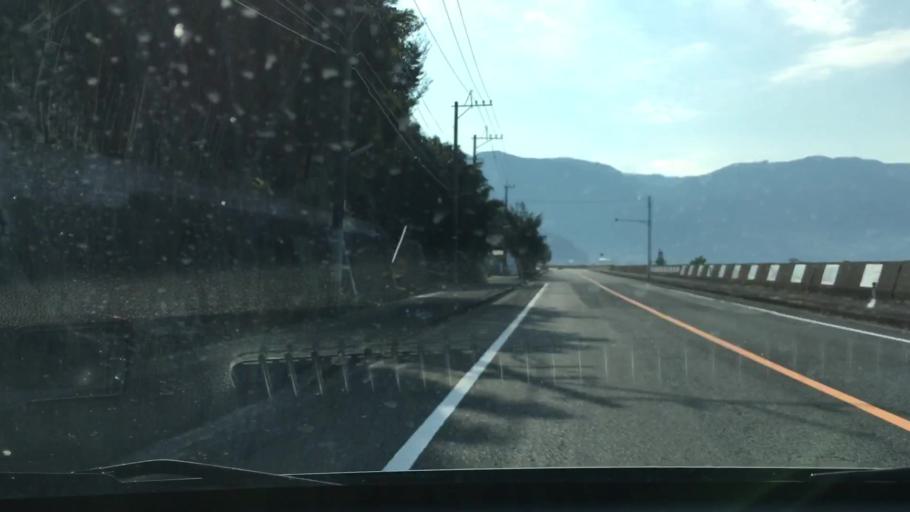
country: JP
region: Kagoshima
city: Kokubu-matsuki
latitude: 31.6674
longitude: 130.8196
